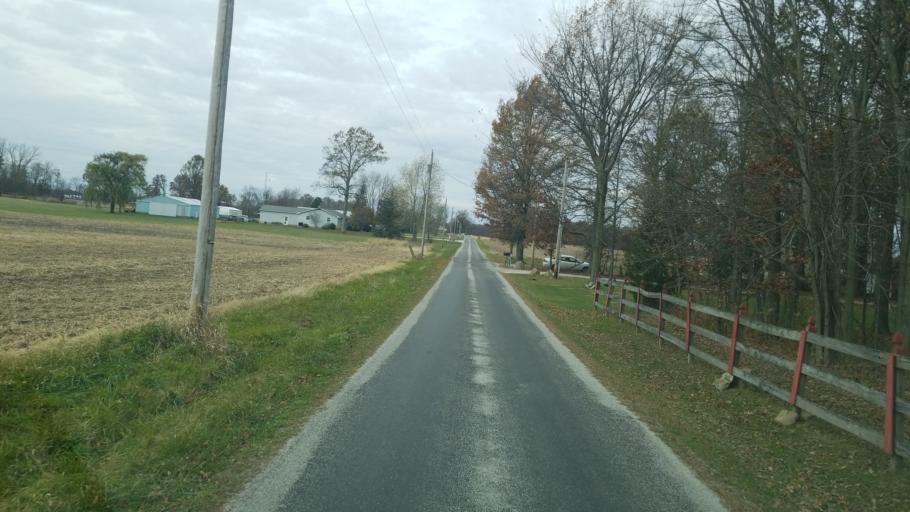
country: US
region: Ohio
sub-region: Morrow County
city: Cardington
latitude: 40.5504
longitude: -82.9807
